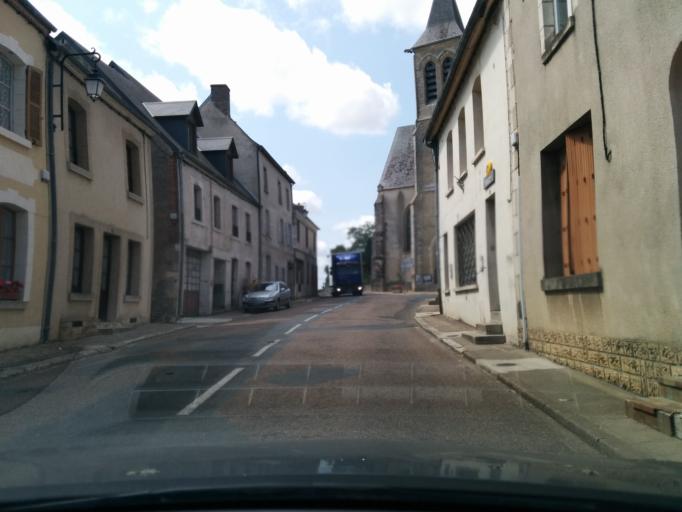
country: FR
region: Centre
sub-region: Departement du Cher
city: Henrichemont
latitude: 47.3448
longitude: 2.4856
